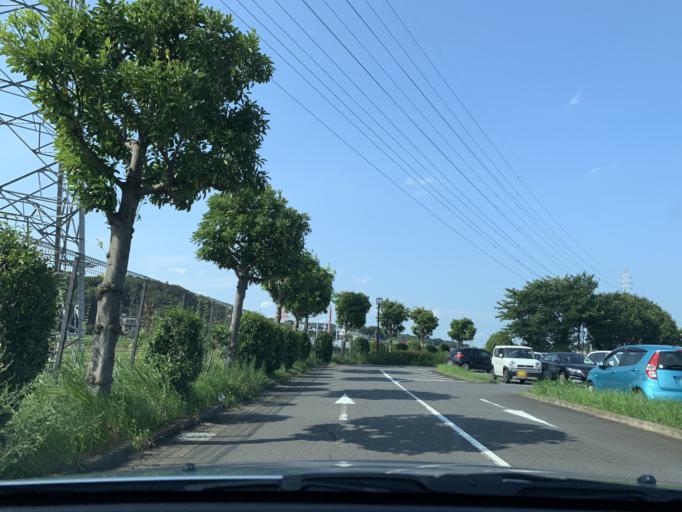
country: JP
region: Chiba
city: Nagareyama
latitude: 35.8504
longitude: 139.9310
